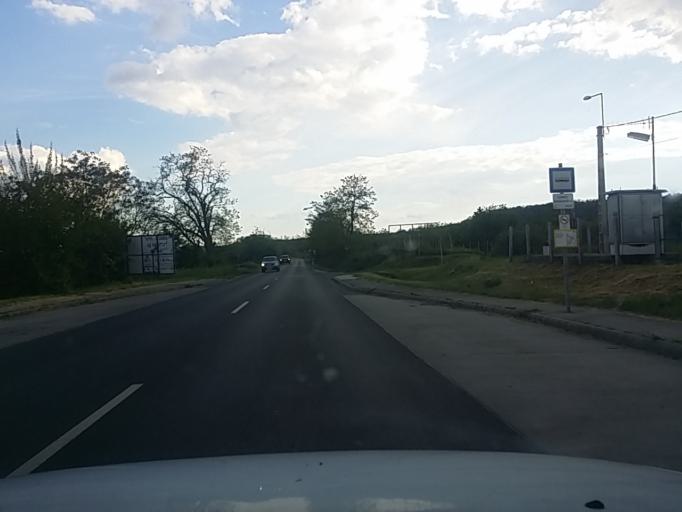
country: HU
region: Pest
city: Mogyorod
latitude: 47.6476
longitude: 19.2347
